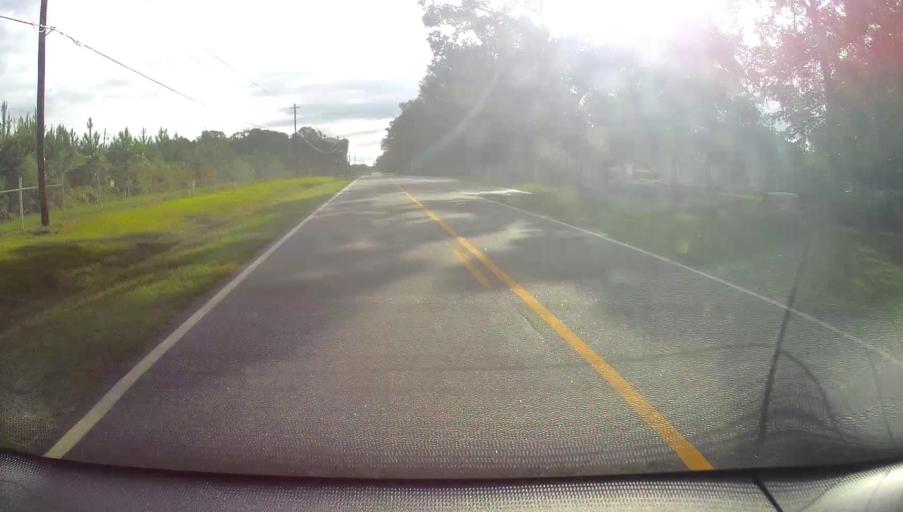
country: US
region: Georgia
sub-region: Peach County
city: Byron
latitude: 32.6514
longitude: -83.7262
